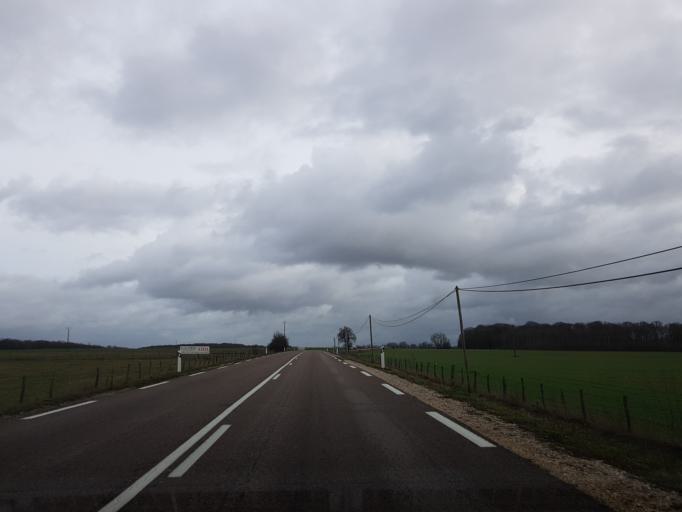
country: FR
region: Champagne-Ardenne
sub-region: Departement de la Haute-Marne
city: Fayl-Billot
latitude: 47.7705
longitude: 5.6979
